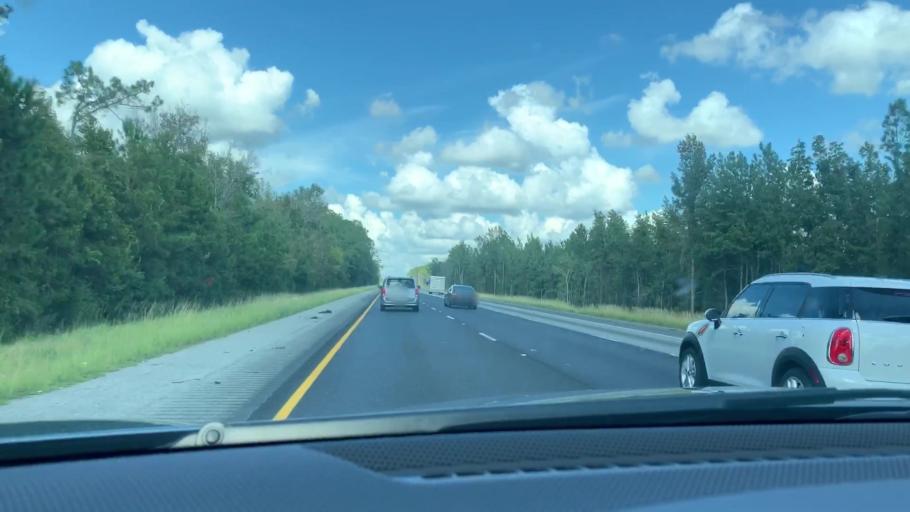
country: US
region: Georgia
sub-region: Camden County
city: Woodbine
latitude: 30.9151
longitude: -81.6859
